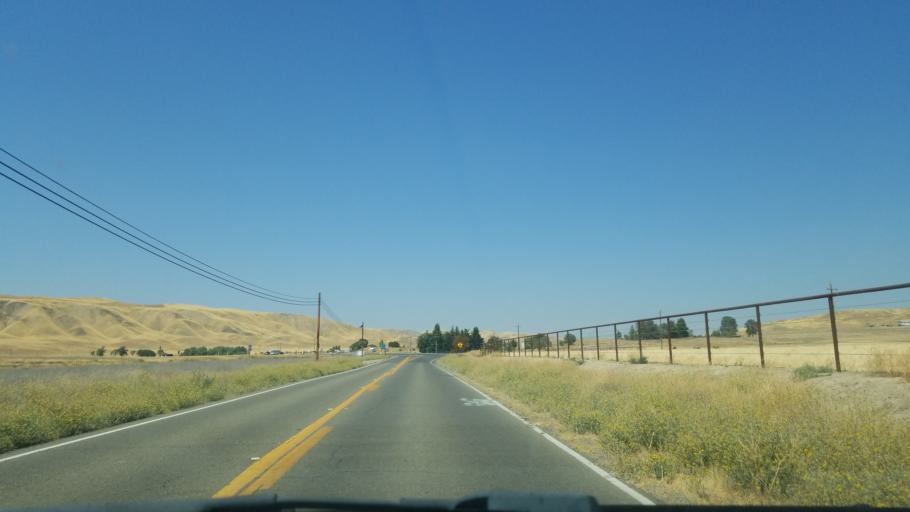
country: US
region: California
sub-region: San Luis Obispo County
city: Shandon
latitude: 35.6632
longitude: -120.3605
